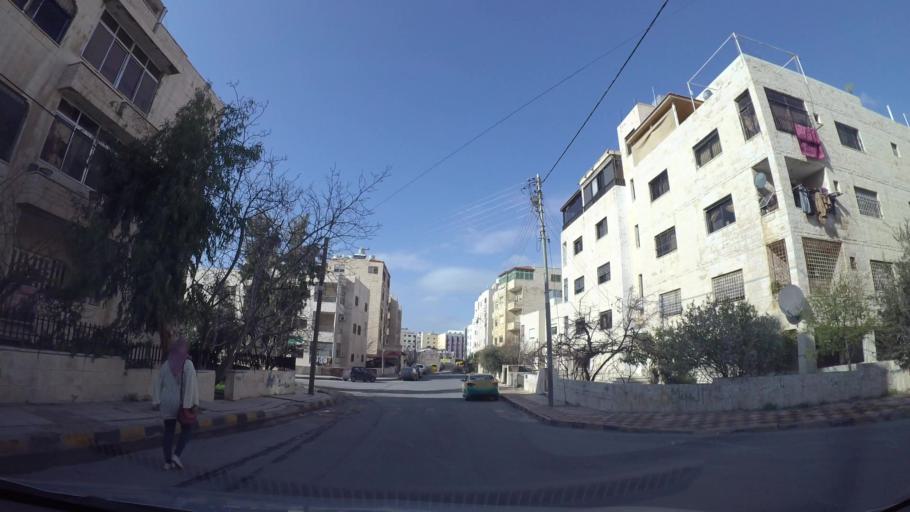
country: JO
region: Amman
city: Al Jubayhah
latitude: 32.0217
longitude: 35.8513
